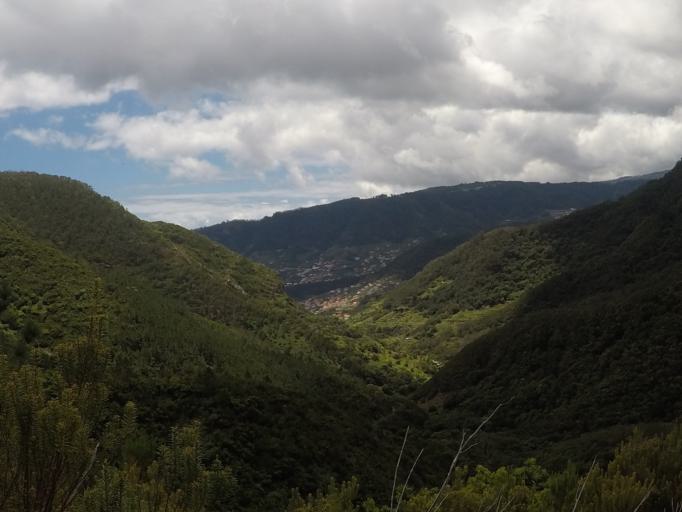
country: PT
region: Madeira
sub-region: Machico
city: Canical
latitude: 32.7546
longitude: -16.7689
